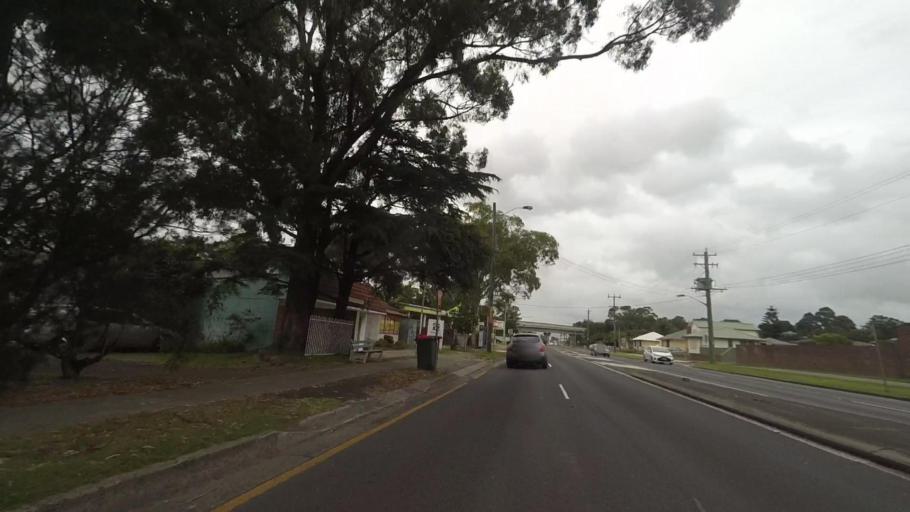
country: AU
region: New South Wales
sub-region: Wollongong
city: Cordeaux Heights
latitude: -34.4594
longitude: 150.8407
